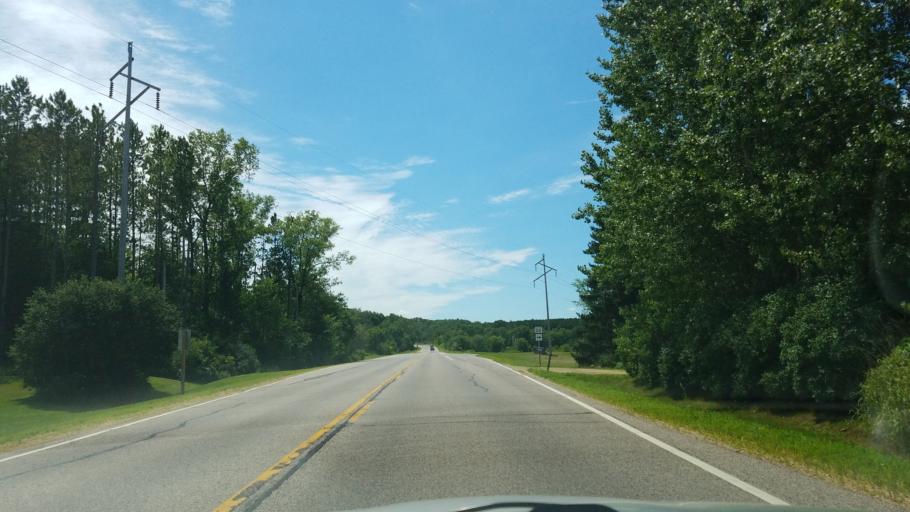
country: US
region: Wisconsin
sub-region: Saint Croix County
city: Glenwood City
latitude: 45.0324
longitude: -92.1879
